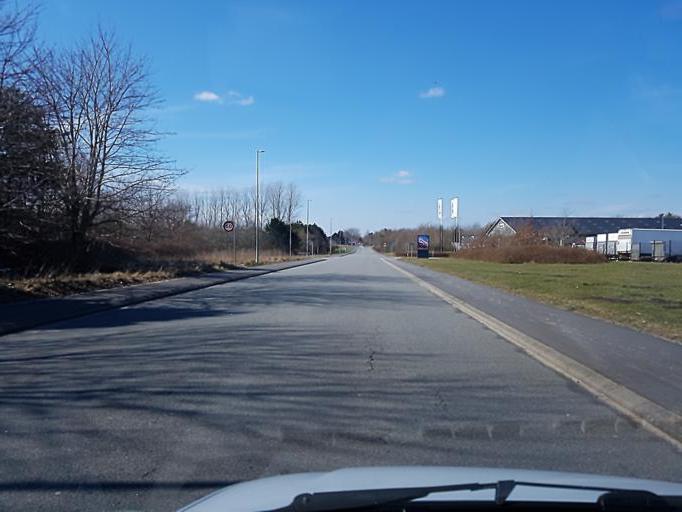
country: DK
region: South Denmark
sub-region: Varde Kommune
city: Varde
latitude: 55.6083
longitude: 8.5035
